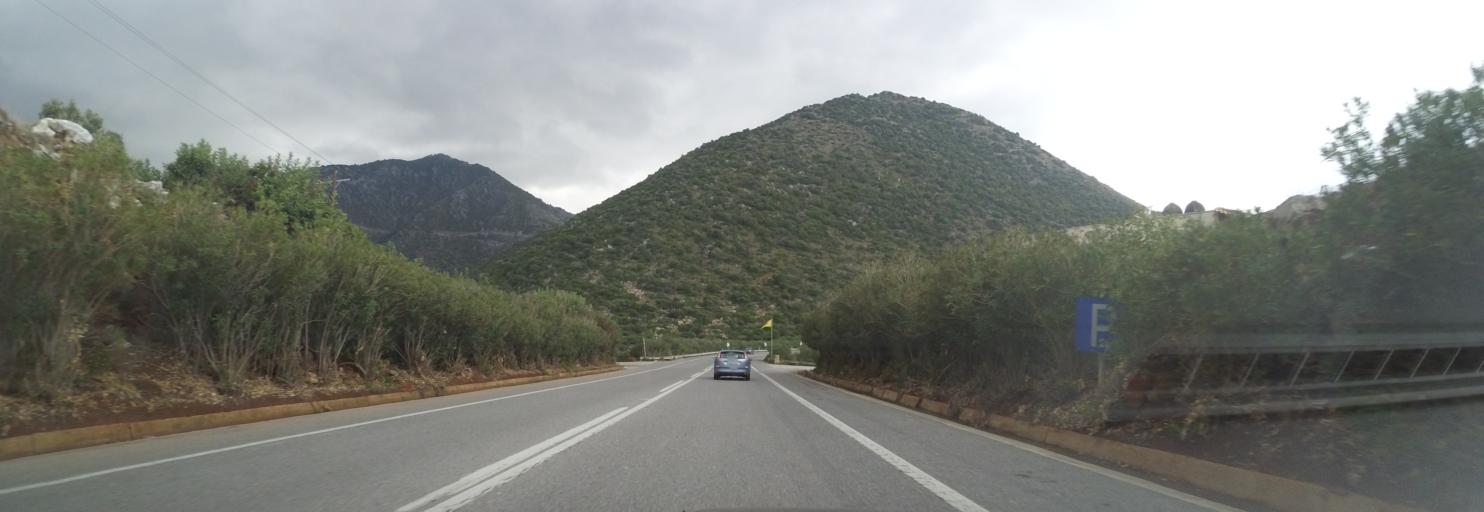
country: GR
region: Crete
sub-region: Nomos Rethymnis
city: Zoniana
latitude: 35.4064
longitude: 24.8177
